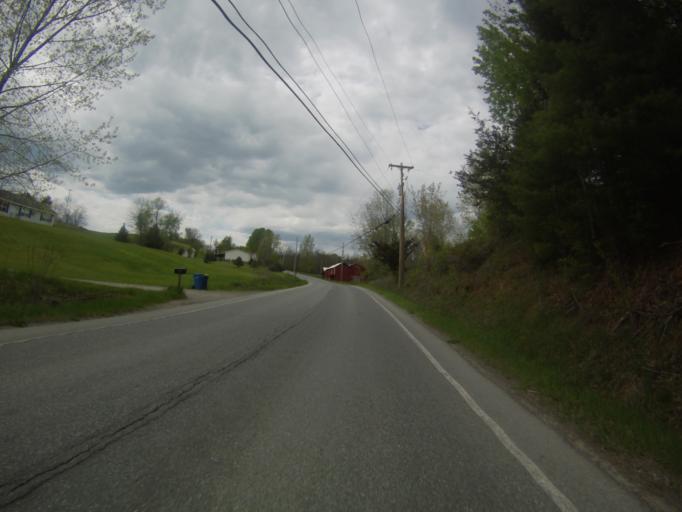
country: US
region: New York
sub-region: Essex County
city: Port Henry
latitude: 43.9491
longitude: -73.4739
